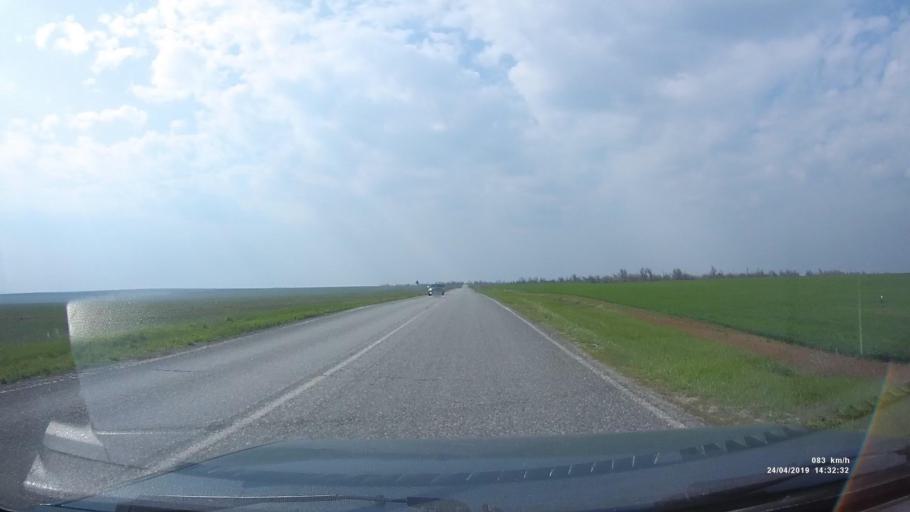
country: RU
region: Kalmykiya
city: Arshan'
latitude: 46.3655
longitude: 43.9673
